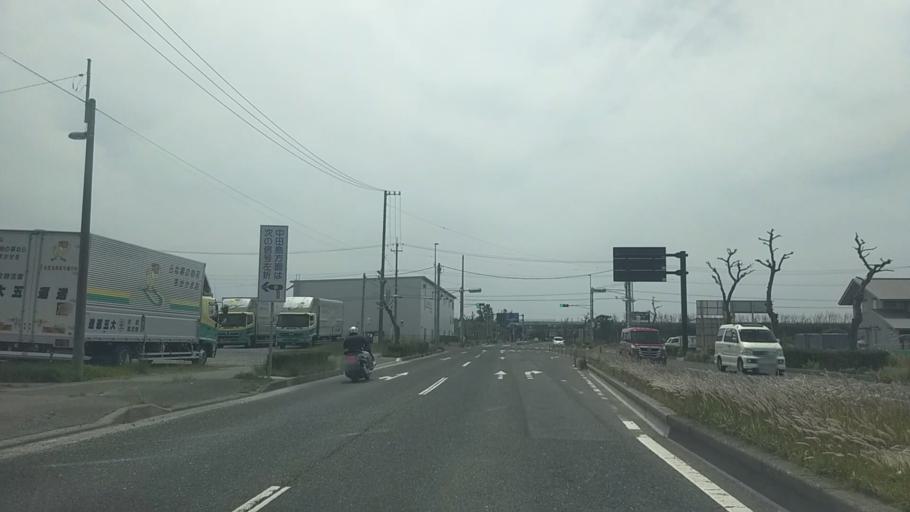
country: JP
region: Shizuoka
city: Hamamatsu
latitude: 34.6788
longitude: 137.6481
